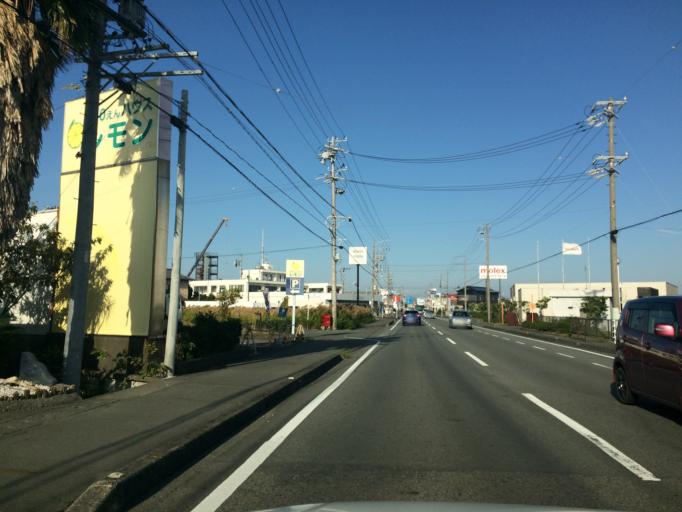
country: JP
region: Shizuoka
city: Shimada
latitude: 34.7629
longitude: 138.2472
